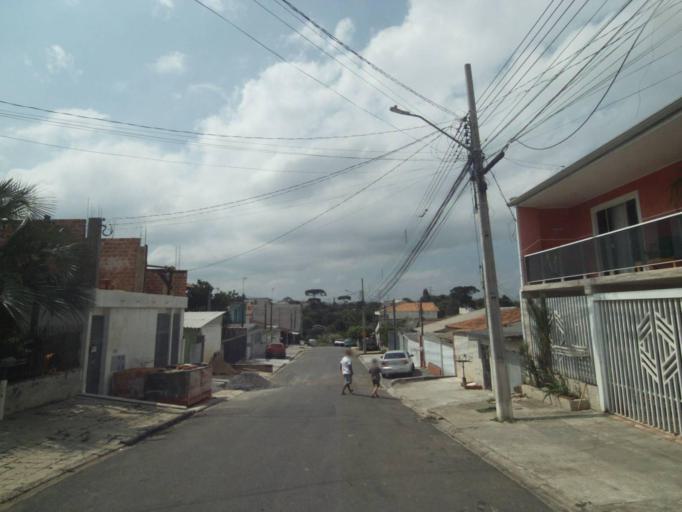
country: BR
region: Parana
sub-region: Curitiba
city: Curitiba
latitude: -25.4990
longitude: -49.3439
